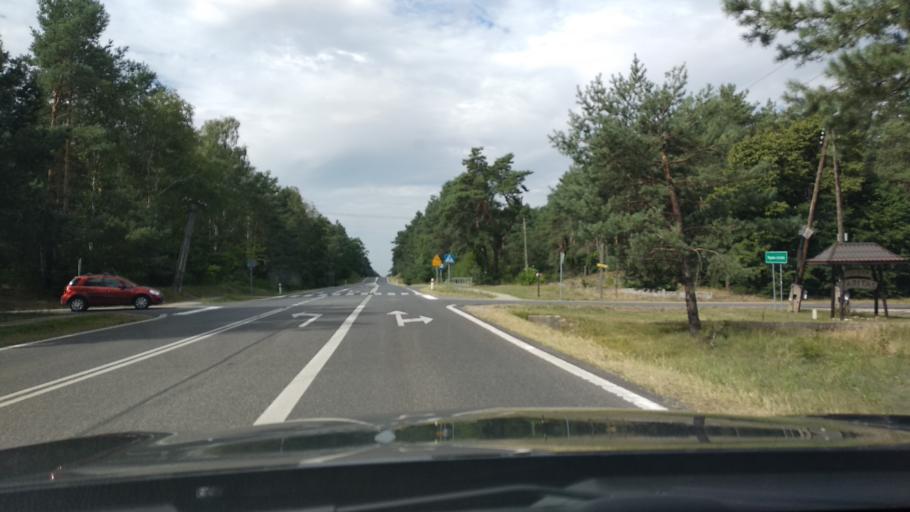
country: PL
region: Masovian Voivodeship
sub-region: Powiat pultuski
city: Zatory
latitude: 52.5435
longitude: 21.1476
